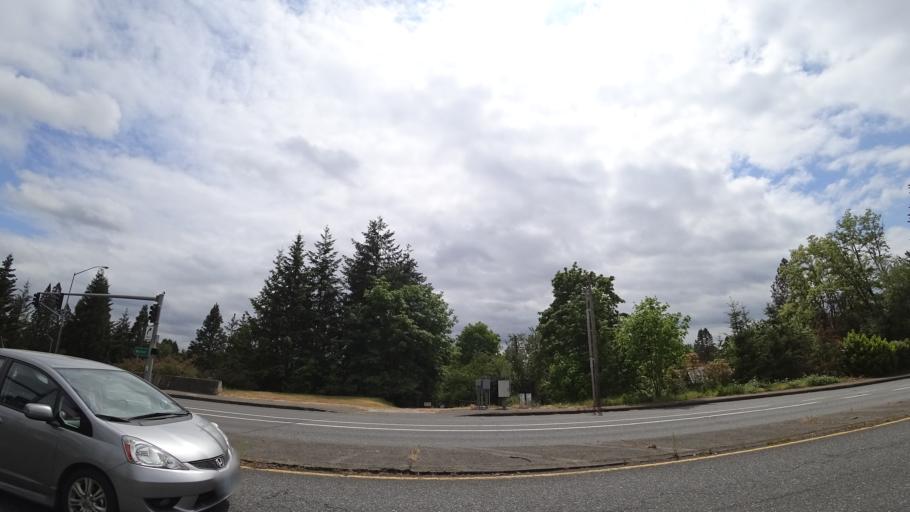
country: US
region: Oregon
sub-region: Washington County
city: Cedar Hills
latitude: 45.4990
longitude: -122.7916
